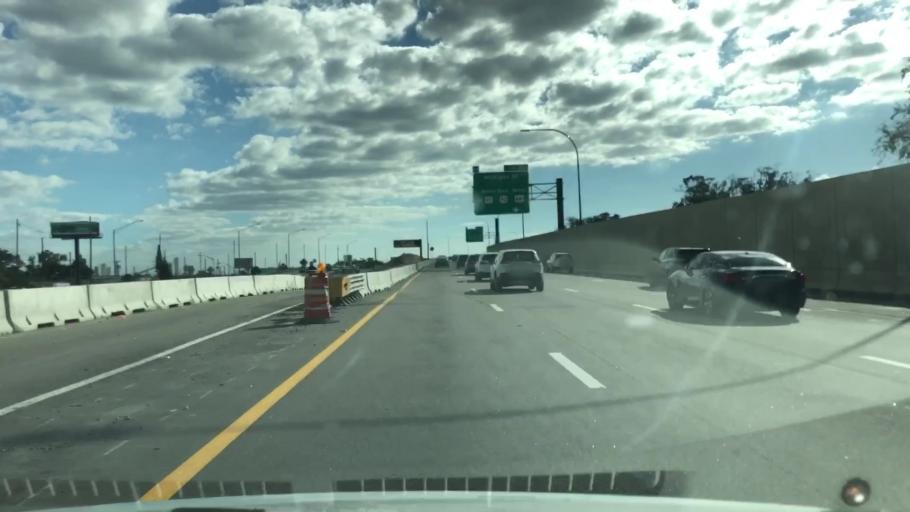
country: US
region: Florida
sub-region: Orange County
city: Orlando
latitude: 28.5236
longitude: -81.3865
